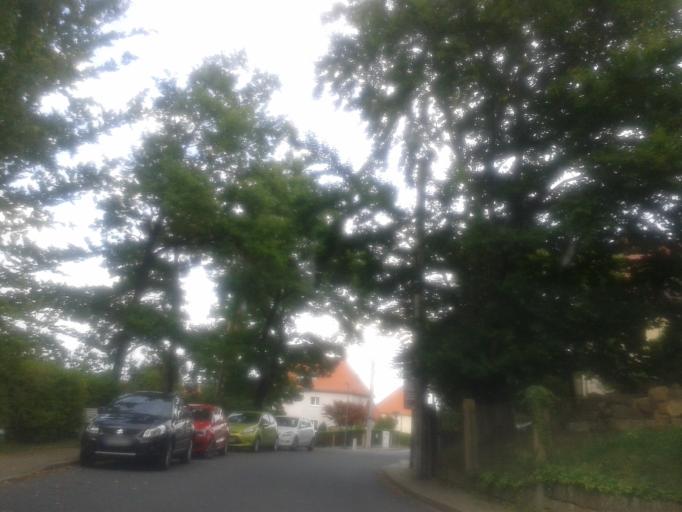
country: DE
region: Saxony
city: Albertstadt
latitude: 51.0531
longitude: 13.8324
